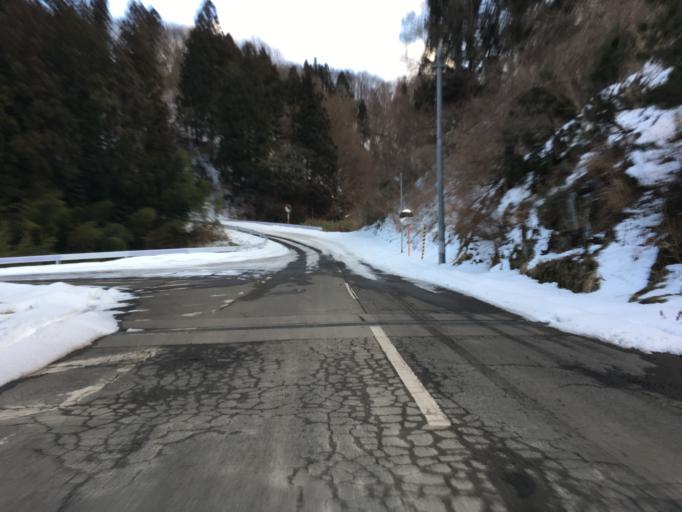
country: JP
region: Fukushima
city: Fukushima-shi
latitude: 37.6391
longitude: 140.5875
